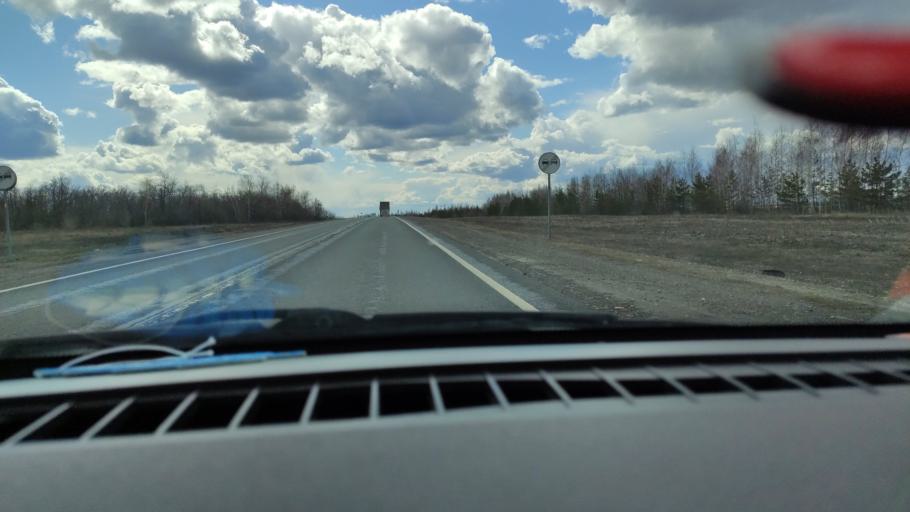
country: RU
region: Samara
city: Syzran'
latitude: 52.8640
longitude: 48.2690
